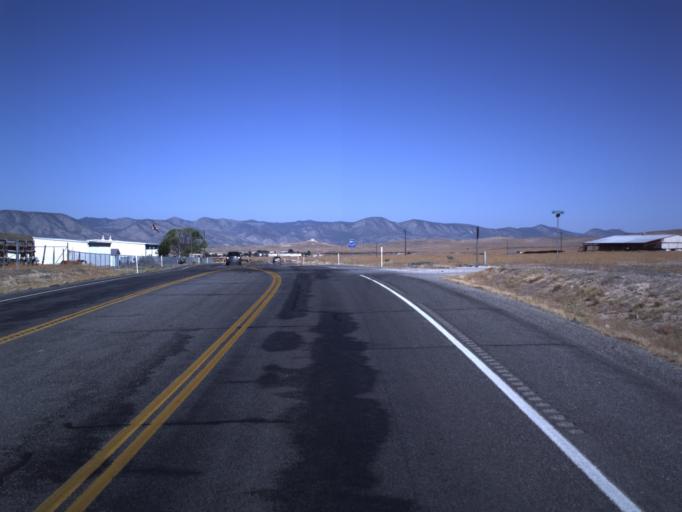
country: US
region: Utah
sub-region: Sanpete County
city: Gunnison
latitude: 39.1584
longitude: -111.7799
